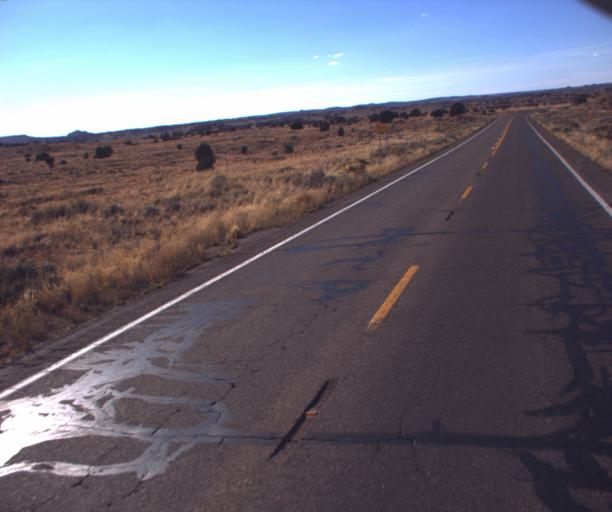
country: US
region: Arizona
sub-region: Coconino County
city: Kaibito
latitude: 36.5803
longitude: -111.1402
